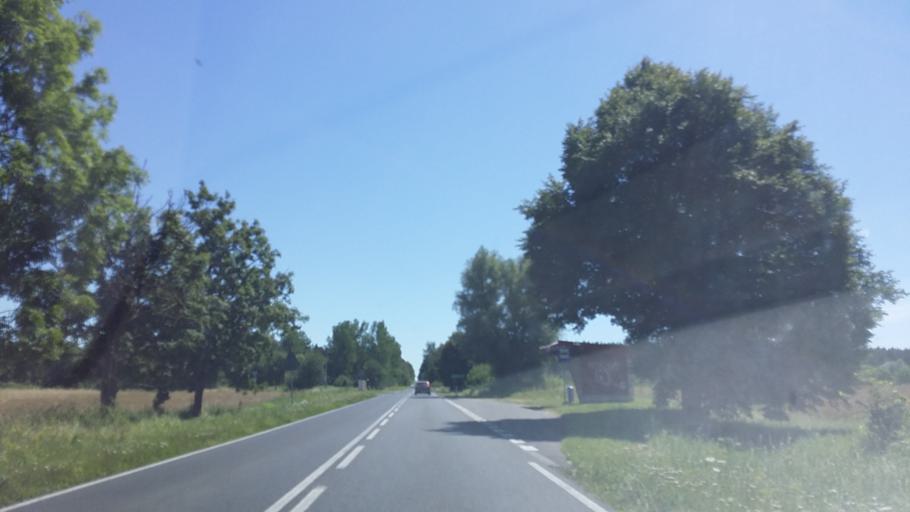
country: PL
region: West Pomeranian Voivodeship
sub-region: Powiat kolobrzeski
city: Kolobrzeg
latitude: 54.1262
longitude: 15.5759
